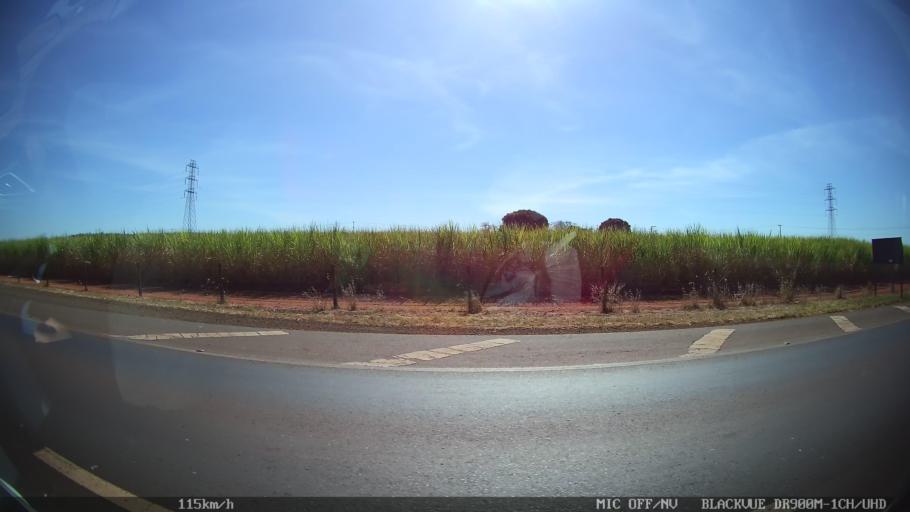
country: BR
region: Sao Paulo
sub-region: Barretos
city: Barretos
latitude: -20.5070
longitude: -48.5528
